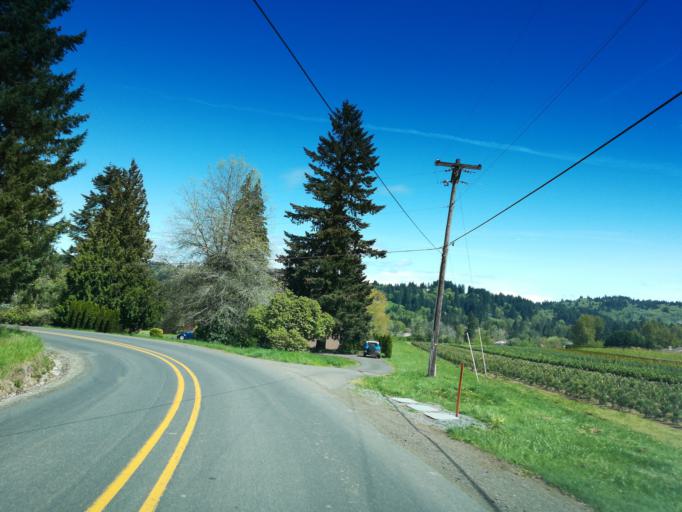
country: US
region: Oregon
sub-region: Clackamas County
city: Damascus
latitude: 45.4469
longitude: -122.4223
